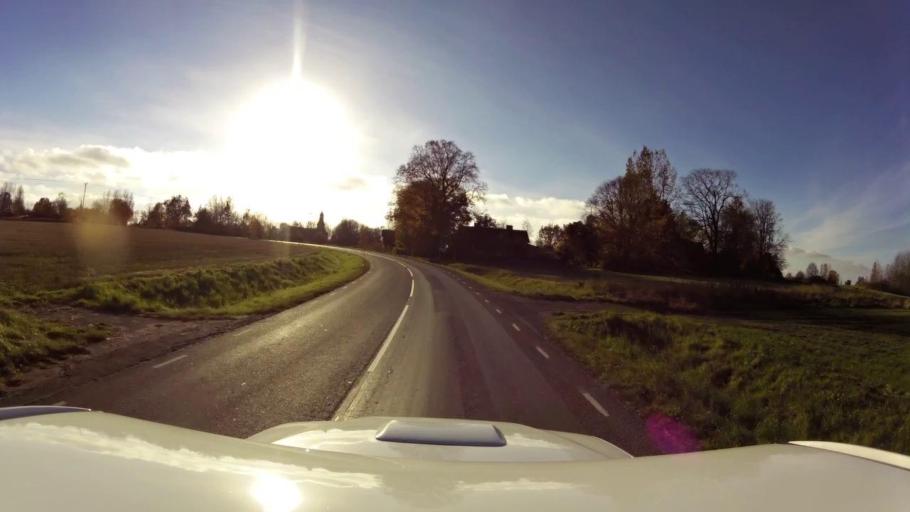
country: SE
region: OEstergoetland
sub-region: Linkopings Kommun
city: Vikingstad
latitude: 58.2921
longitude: 15.4522
